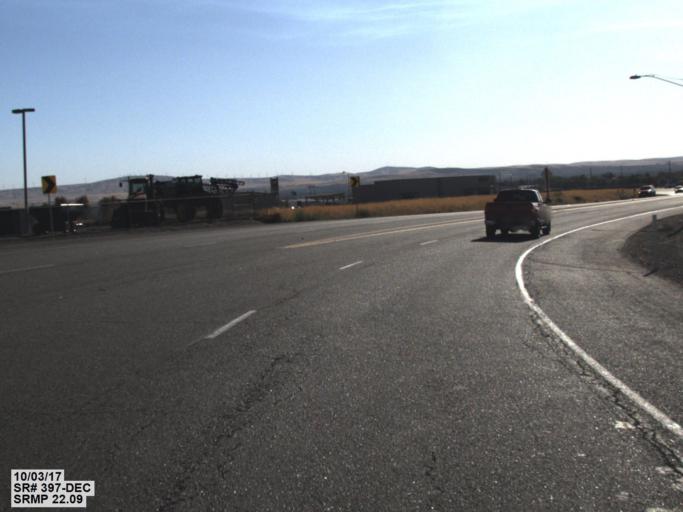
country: US
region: Washington
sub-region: Franklin County
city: Pasco
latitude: 46.2484
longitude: -119.0825
